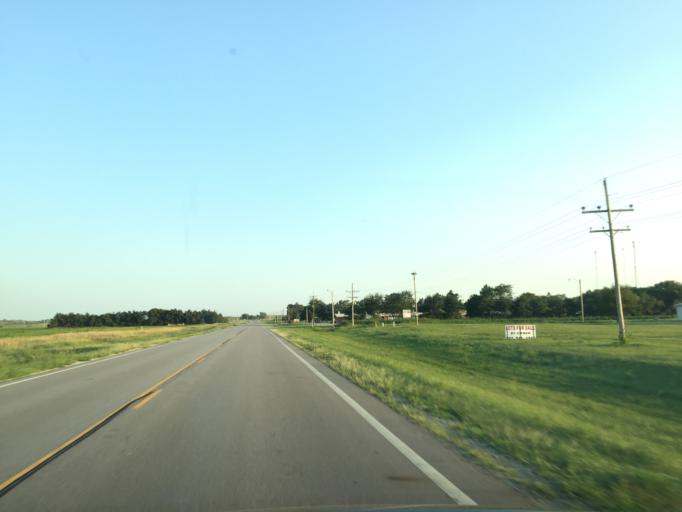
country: US
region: Kansas
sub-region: Ellsworth County
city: Ellsworth
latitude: 38.7212
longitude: -98.2345
